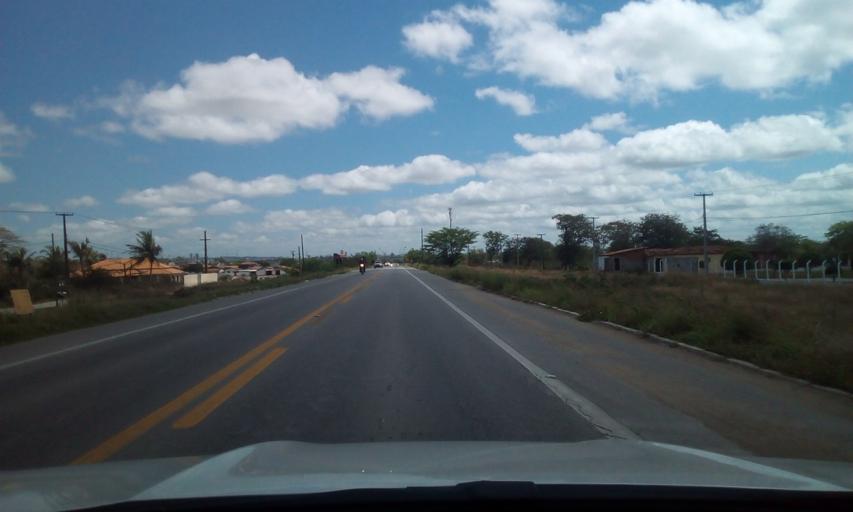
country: BR
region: Paraiba
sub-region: Campina Grande
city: Campina Grande
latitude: -7.2981
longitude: -35.8917
